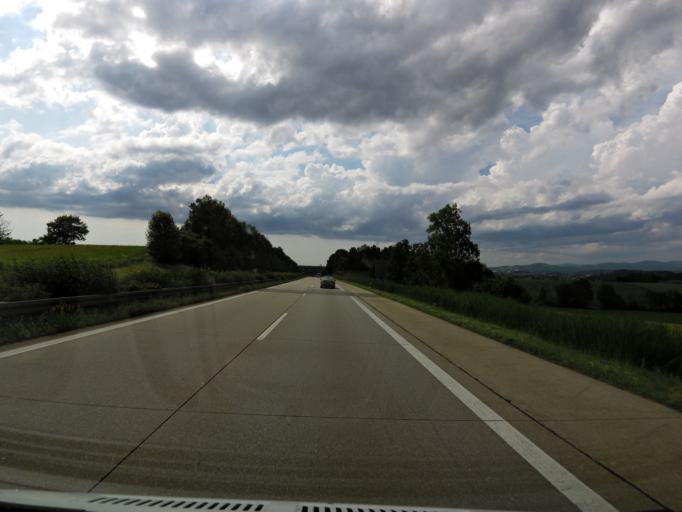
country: DE
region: Bavaria
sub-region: Lower Bavaria
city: Winzer
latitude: 48.7518
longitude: 13.0849
